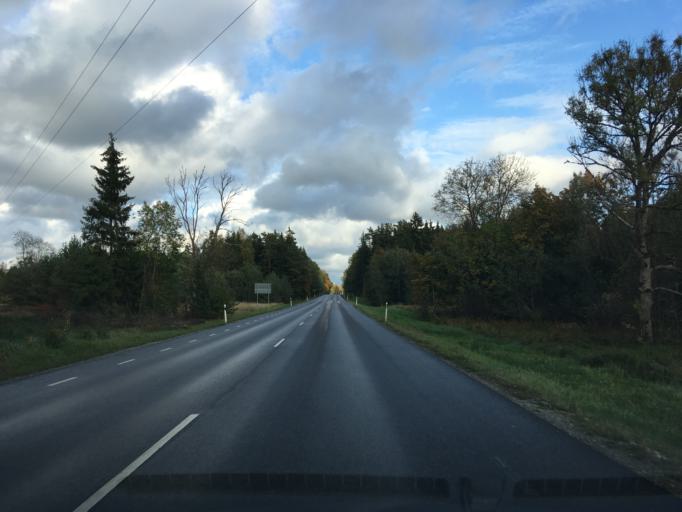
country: EE
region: Harju
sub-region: Nissi vald
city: Turba
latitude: 59.2299
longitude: 24.1855
